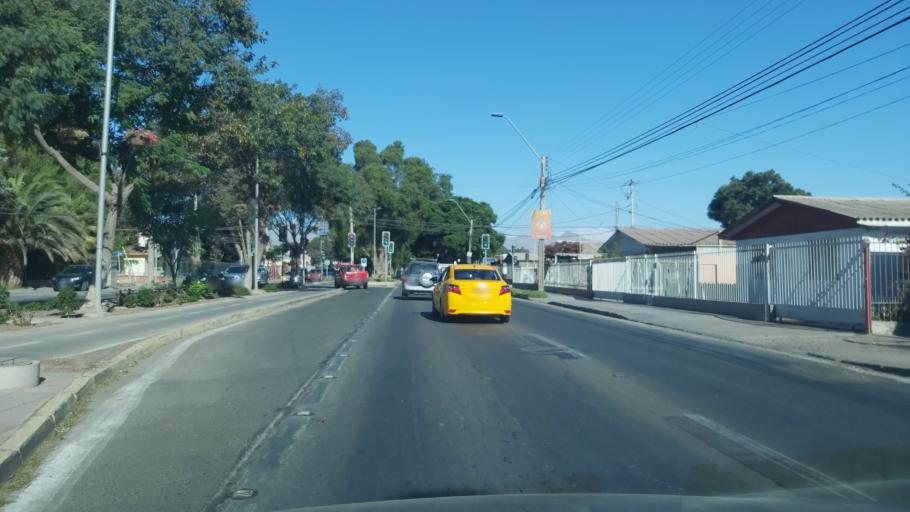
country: CL
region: Atacama
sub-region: Provincia de Copiapo
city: Copiapo
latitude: -27.3753
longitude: -70.3254
